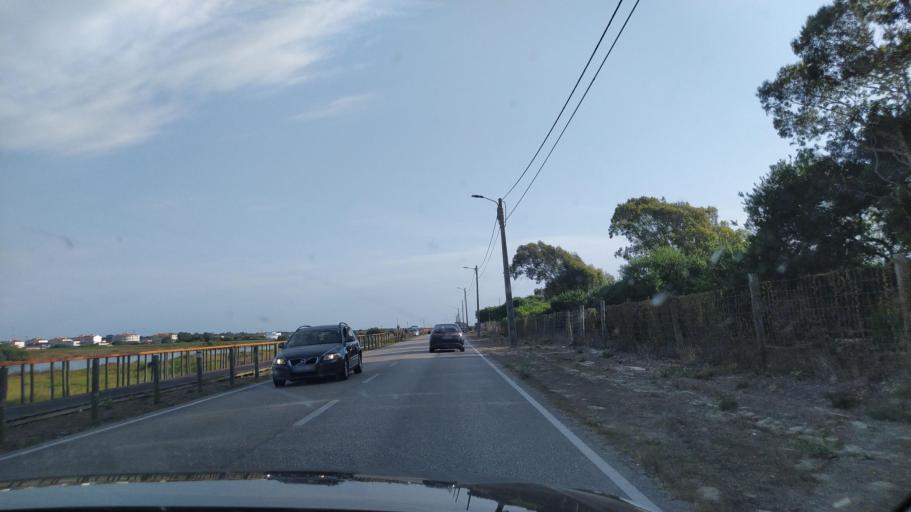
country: PT
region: Aveiro
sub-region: Ilhavo
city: Gafanha da Encarnacao
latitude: 40.5671
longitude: -8.7569
